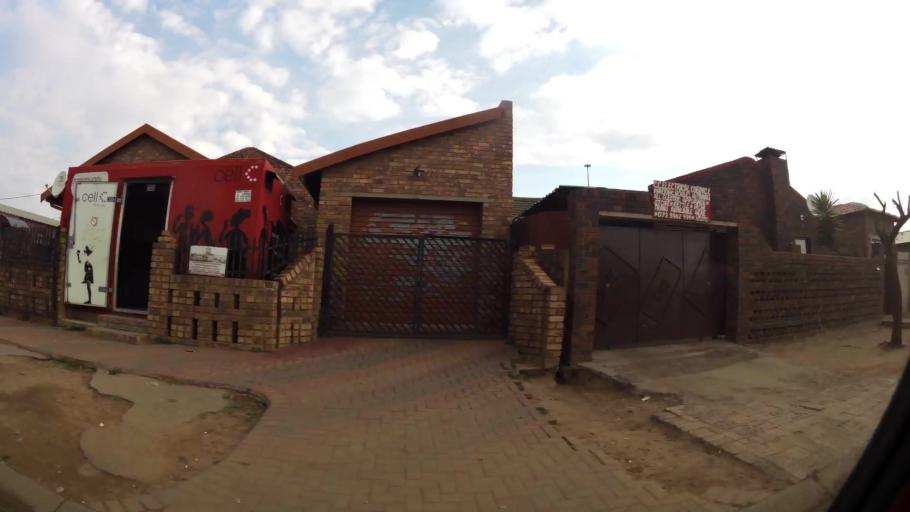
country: ZA
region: Gauteng
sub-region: Sedibeng District Municipality
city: Vanderbijlpark
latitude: -26.6763
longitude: 27.8730
